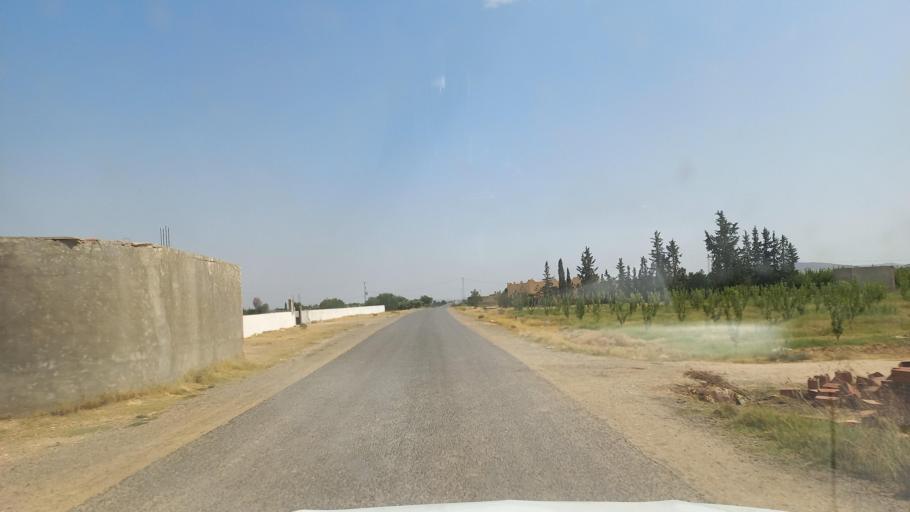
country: TN
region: Al Qasrayn
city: Kasserine
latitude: 35.2453
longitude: 9.0250
